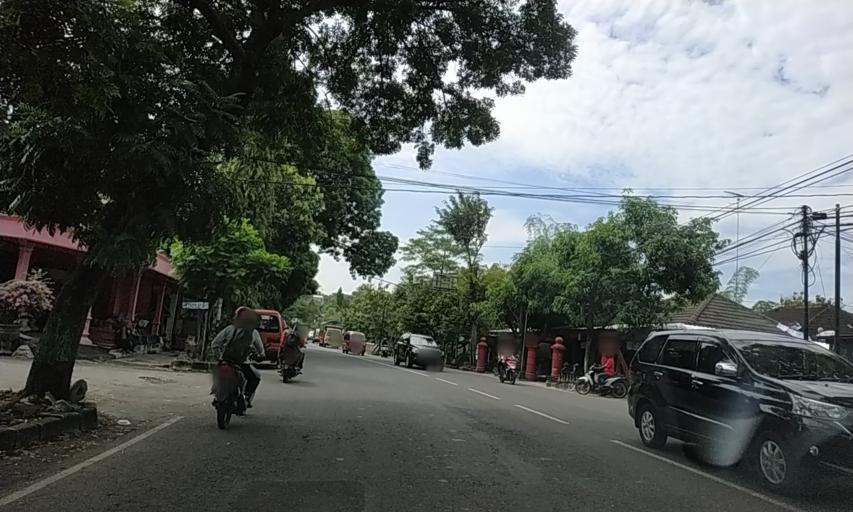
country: ID
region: Central Java
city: Selogiri
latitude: -7.7939
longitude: 110.8996
